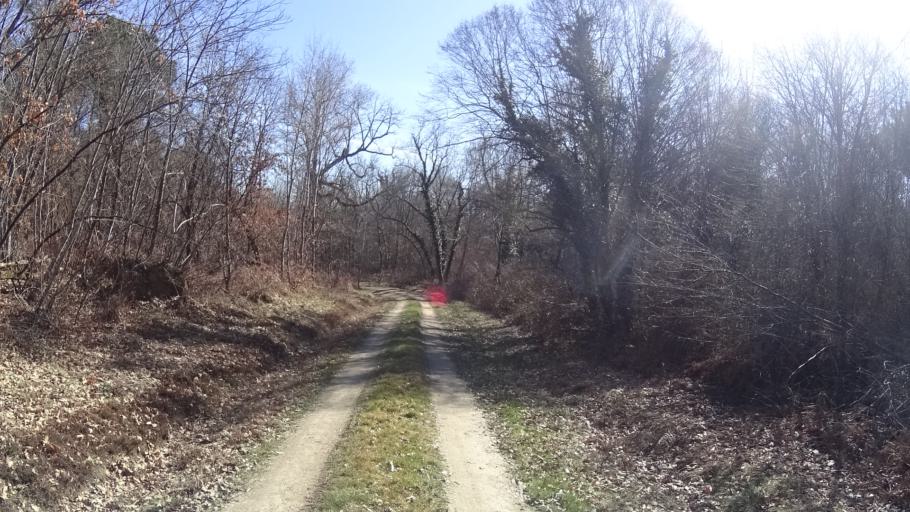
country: FR
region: Aquitaine
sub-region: Departement de la Dordogne
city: Riberac
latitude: 45.1861
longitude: 0.2951
